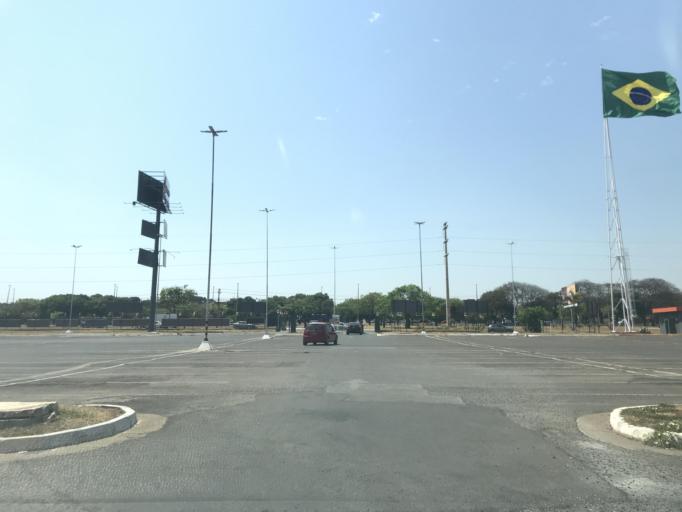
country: BR
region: Federal District
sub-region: Brasilia
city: Brasilia
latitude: -15.7911
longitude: -47.9454
